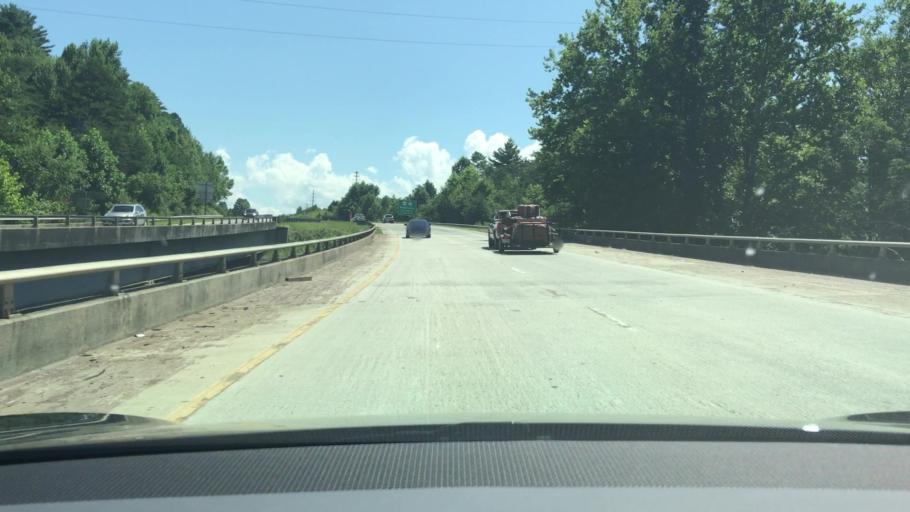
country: US
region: North Carolina
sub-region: Macon County
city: Franklin
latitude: 35.1640
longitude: -83.3757
